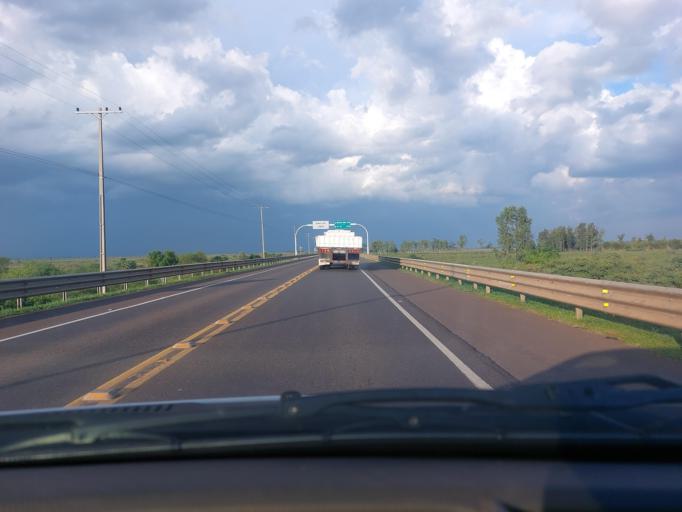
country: PY
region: Cordillera
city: Arroyos y Esteros
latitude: -25.0497
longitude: -57.0832
